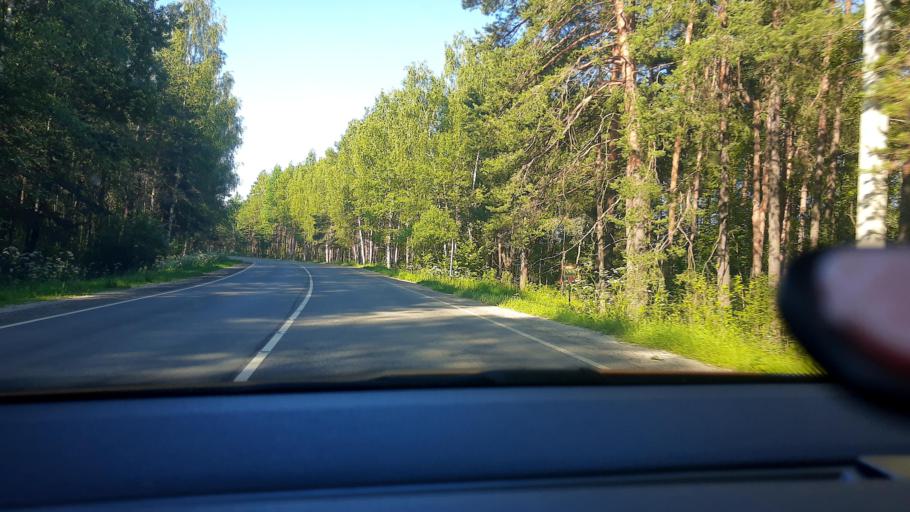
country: RU
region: Moskovskaya
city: Pavlovskiy Posad
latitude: 55.8687
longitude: 38.6812
